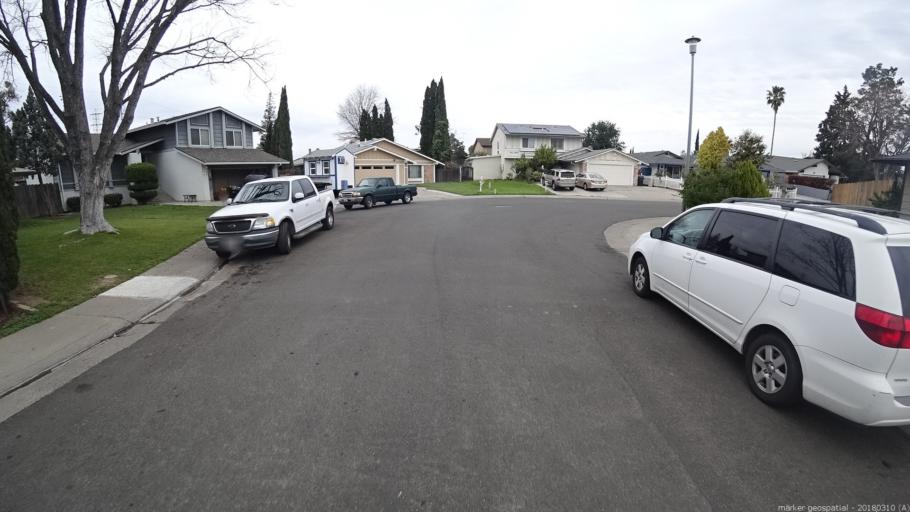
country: US
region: California
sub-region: Sacramento County
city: Florin
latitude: 38.4868
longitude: -121.4074
